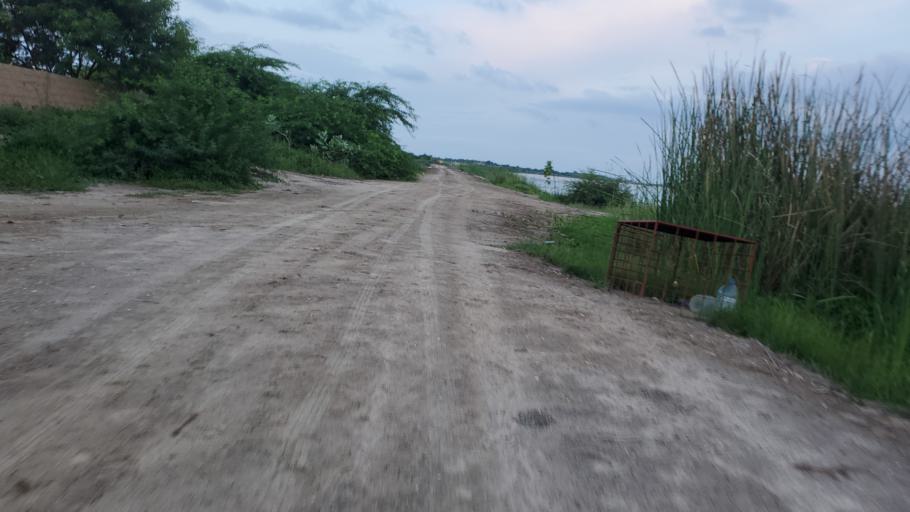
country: SN
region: Saint-Louis
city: Saint-Louis
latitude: 16.0388
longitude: -16.4171
